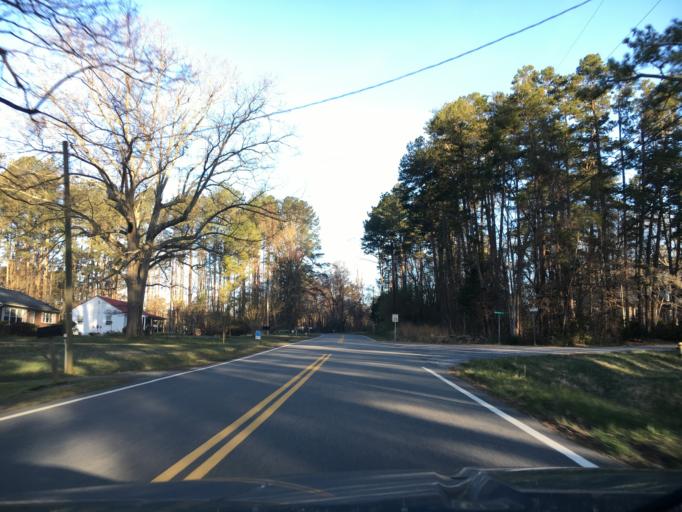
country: US
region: Virginia
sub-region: Halifax County
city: Halifax
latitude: 36.7677
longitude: -78.9174
